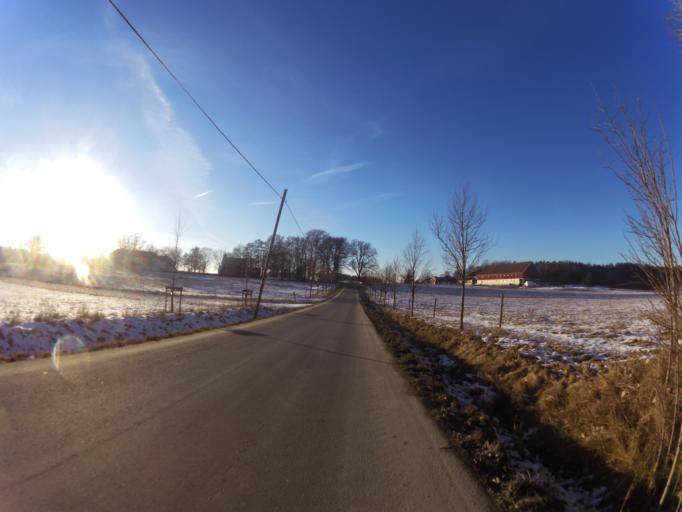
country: NO
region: Ostfold
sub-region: Fredrikstad
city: Lervik
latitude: 59.2530
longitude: 10.8062
